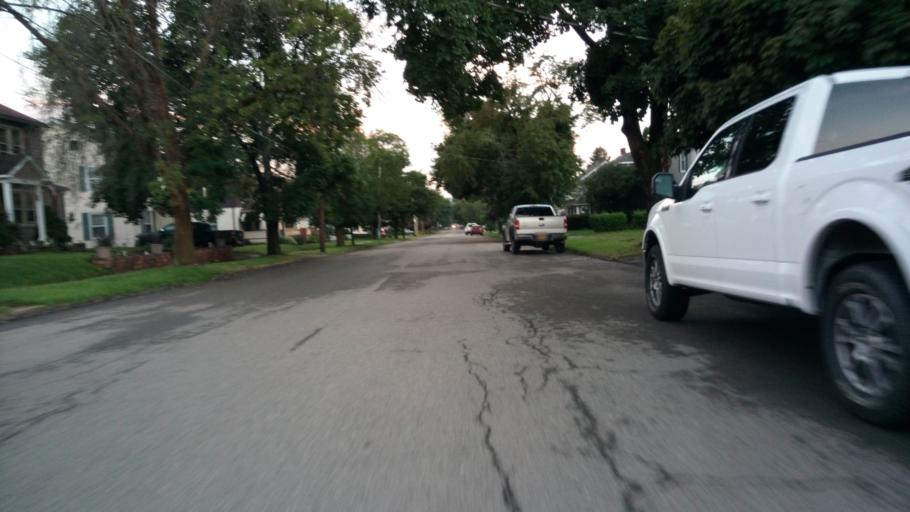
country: US
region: New York
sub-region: Chemung County
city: Elmira
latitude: 42.0986
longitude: -76.8264
